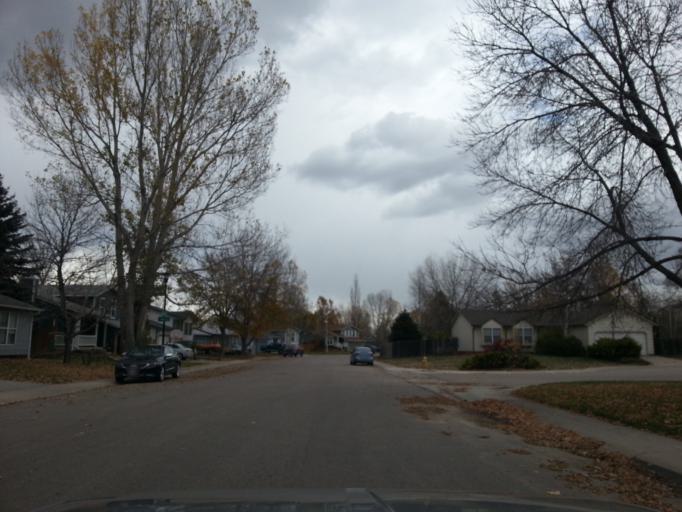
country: US
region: Colorado
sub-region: Larimer County
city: Fort Collins
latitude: 40.5348
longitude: -105.0335
